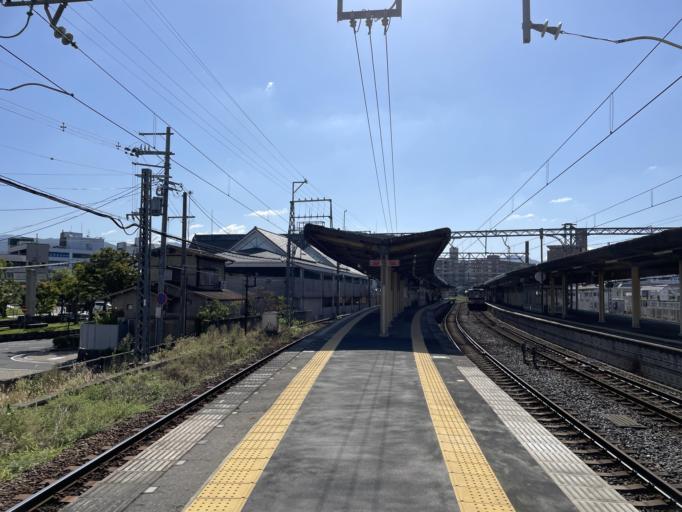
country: JP
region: Nara
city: Kashihara-shi
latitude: 34.4840
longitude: 135.7927
